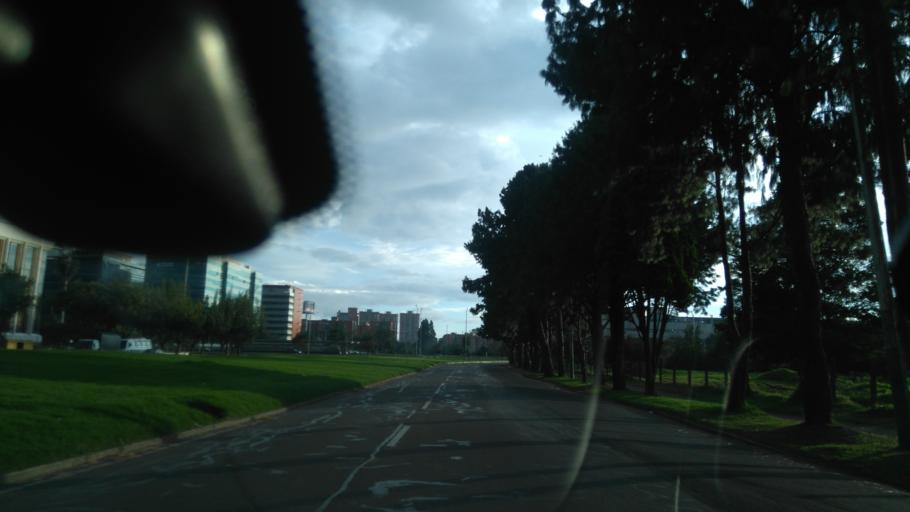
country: CO
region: Bogota D.C.
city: Bogota
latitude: 4.6488
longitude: -74.0978
